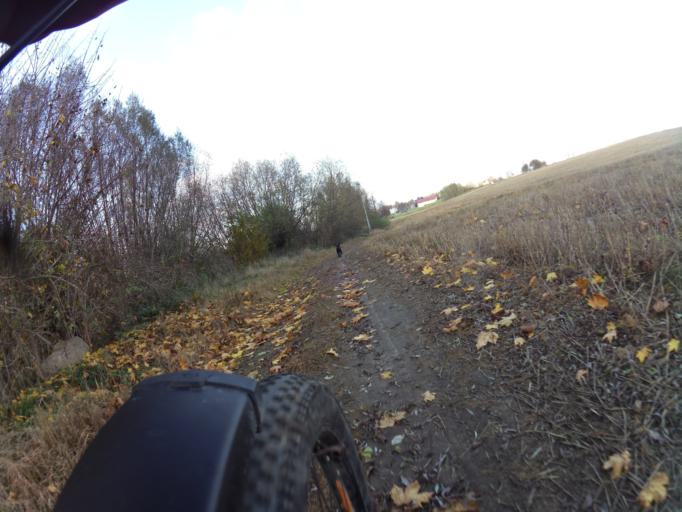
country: PL
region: Pomeranian Voivodeship
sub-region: Powiat pucki
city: Krokowa
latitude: 54.7735
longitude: 18.1710
